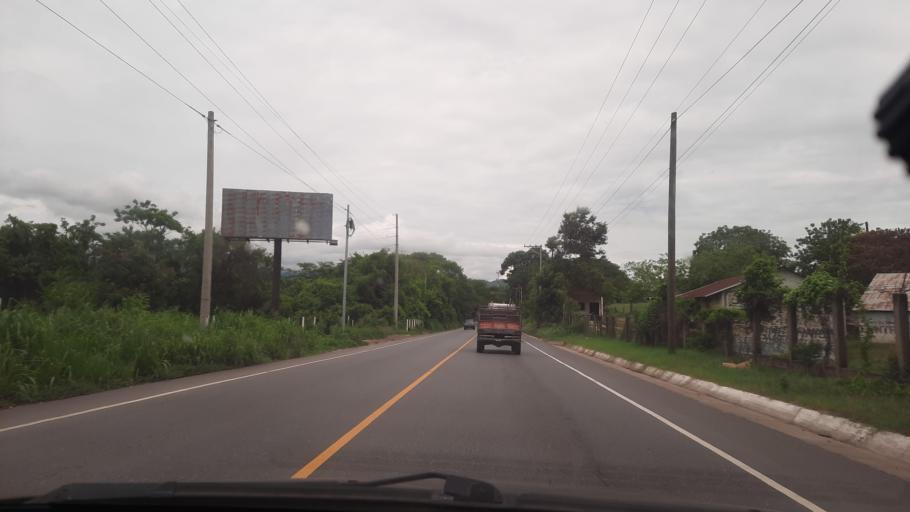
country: GT
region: Zacapa
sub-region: Municipio de Zacapa
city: Gualan
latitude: 15.1340
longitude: -89.3445
